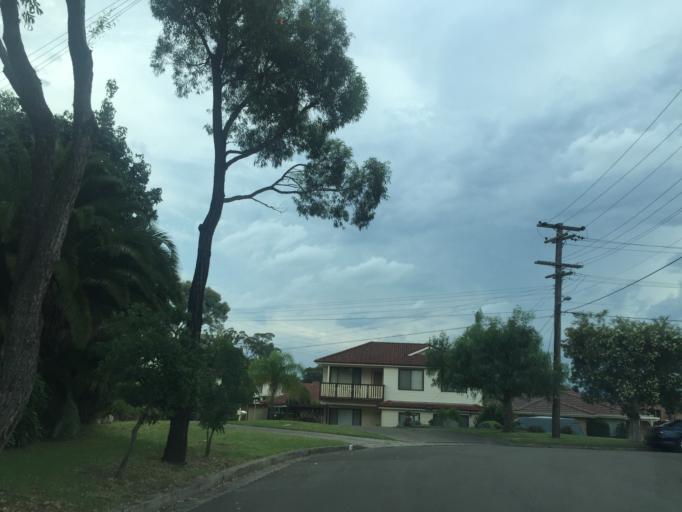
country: AU
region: New South Wales
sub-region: Blacktown
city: Blacktown
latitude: -33.7873
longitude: 150.8970
